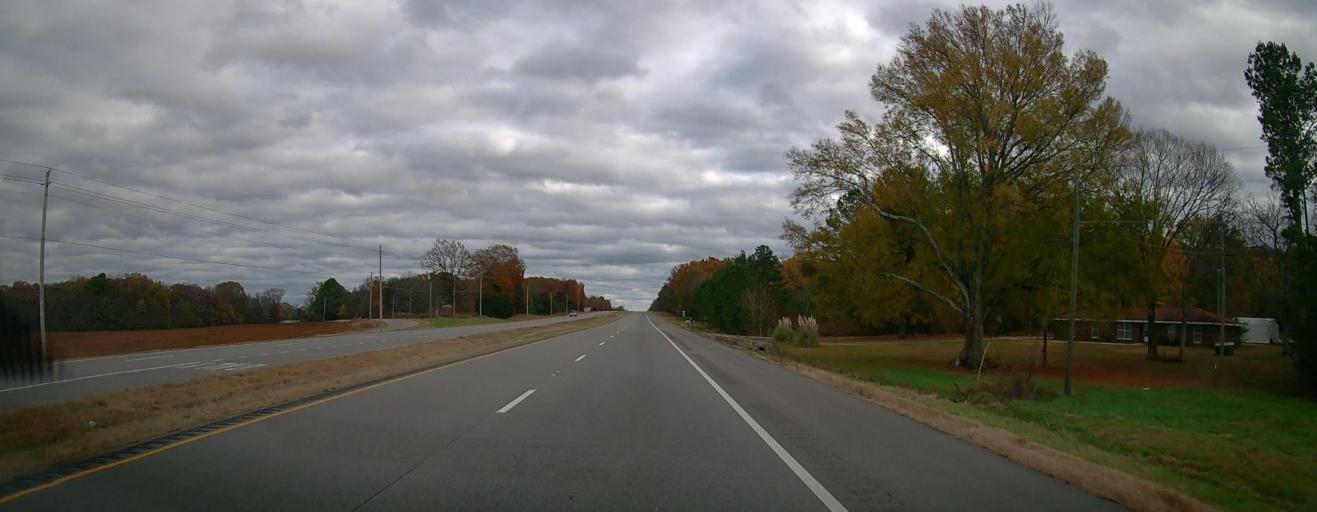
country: US
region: Alabama
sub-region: Colbert County
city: Muscle Shoals
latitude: 34.6706
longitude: -87.5622
